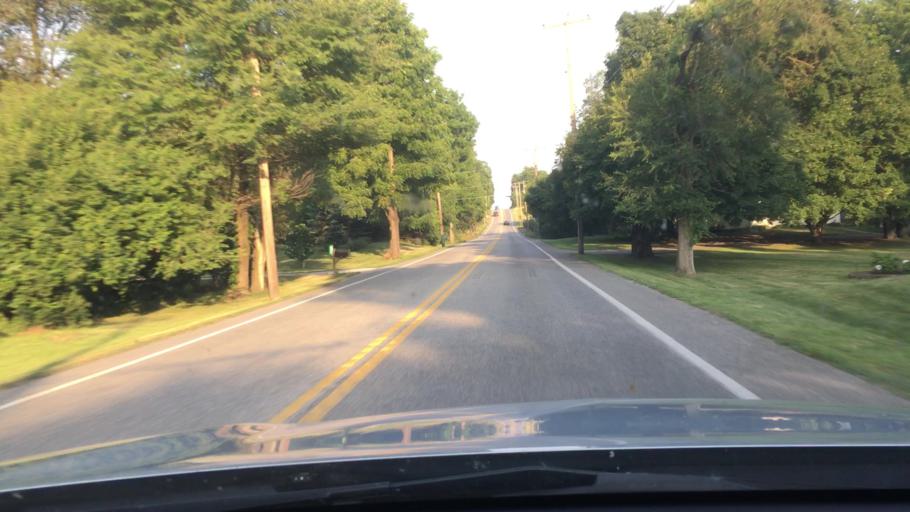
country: US
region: Pennsylvania
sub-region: Cumberland County
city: Boiling Springs
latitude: 40.1740
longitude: -77.1234
